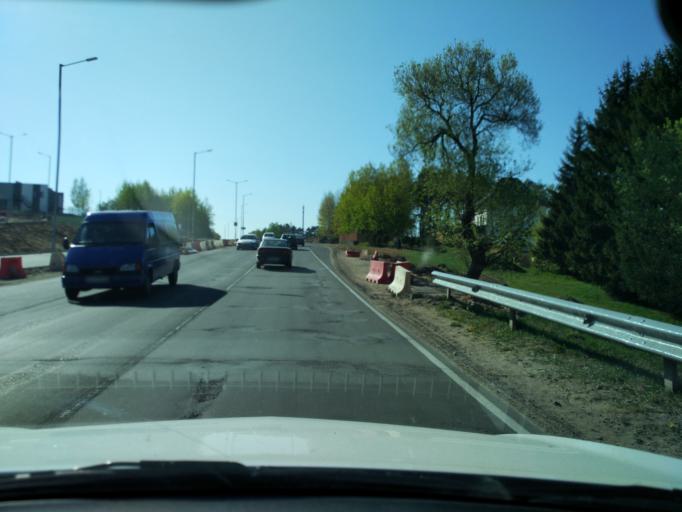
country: BY
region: Minsk
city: Borovlyany
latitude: 53.9645
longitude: 27.6705
